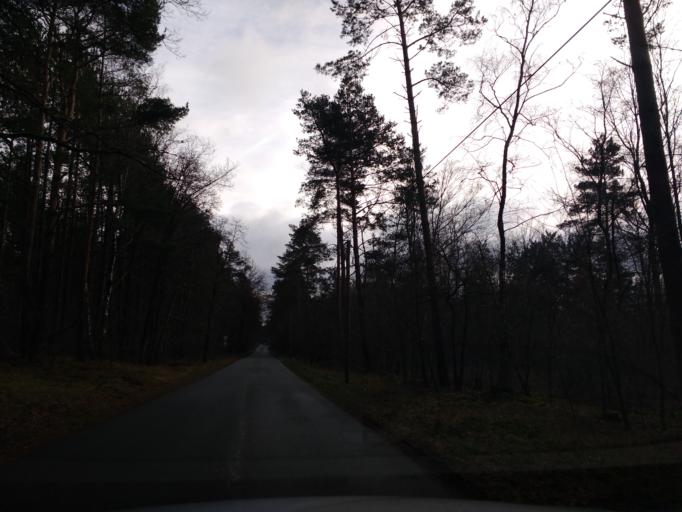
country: DE
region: North Rhine-Westphalia
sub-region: Regierungsbezirk Detmold
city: Hovelhof
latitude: 51.8646
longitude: 8.6812
